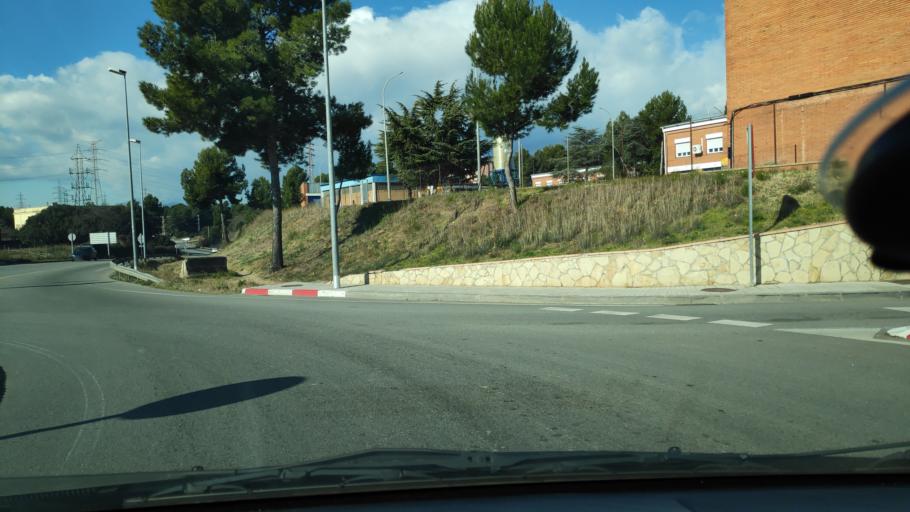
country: ES
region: Catalonia
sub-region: Provincia de Barcelona
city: Sant Quirze del Valles
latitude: 41.5533
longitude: 2.0589
